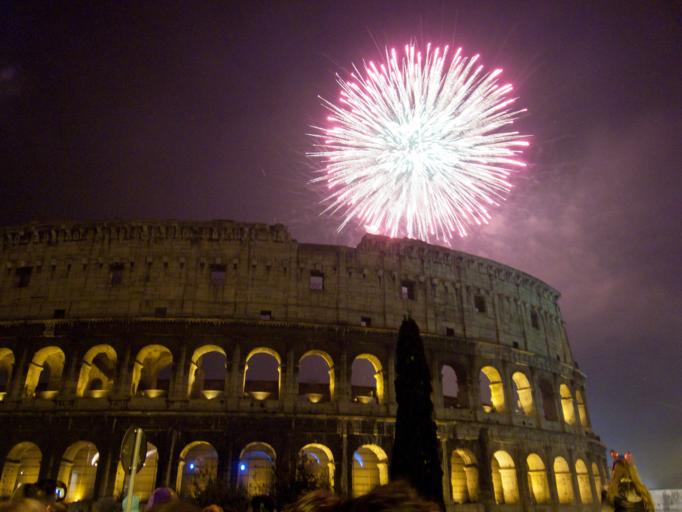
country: IT
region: Latium
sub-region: Citta metropolitana di Roma Capitale
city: Rome
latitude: 41.8917
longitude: 12.4922
